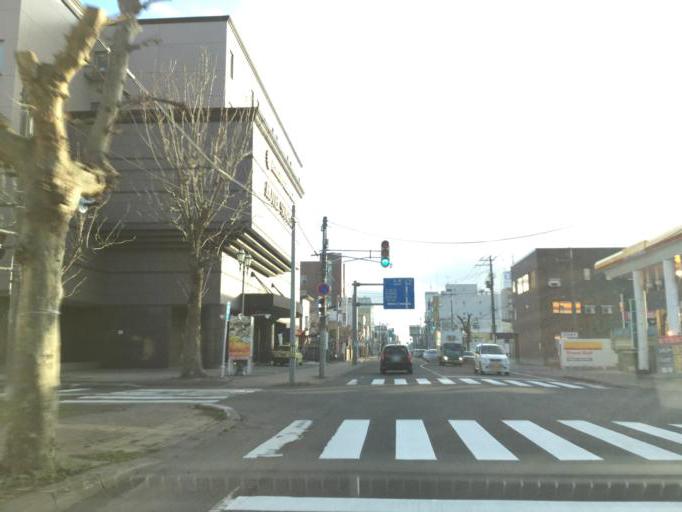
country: JP
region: Hokkaido
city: Iwamizawa
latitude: 43.2042
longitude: 141.7681
